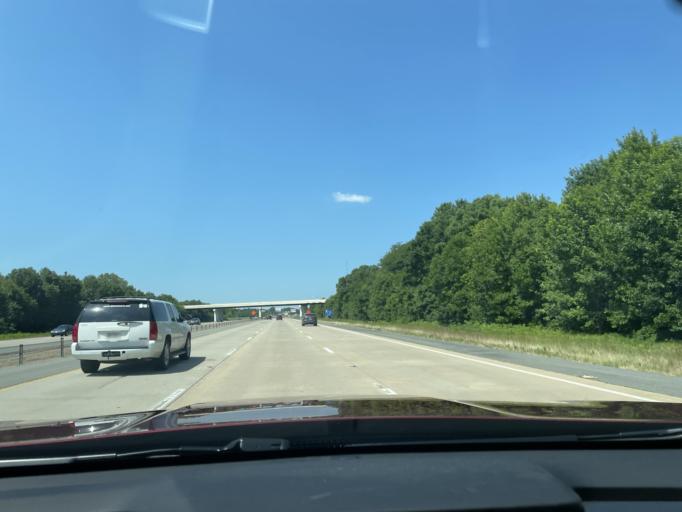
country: US
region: Arkansas
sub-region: Pulaski County
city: McAlmont
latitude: 34.8428
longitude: -92.1556
